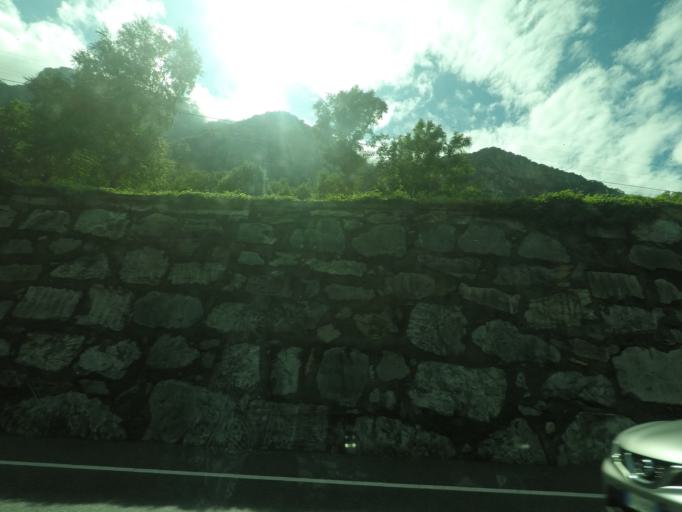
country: IT
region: Aosta Valley
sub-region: Valle d'Aosta
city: Chatillon
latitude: 45.7654
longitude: 7.6036
